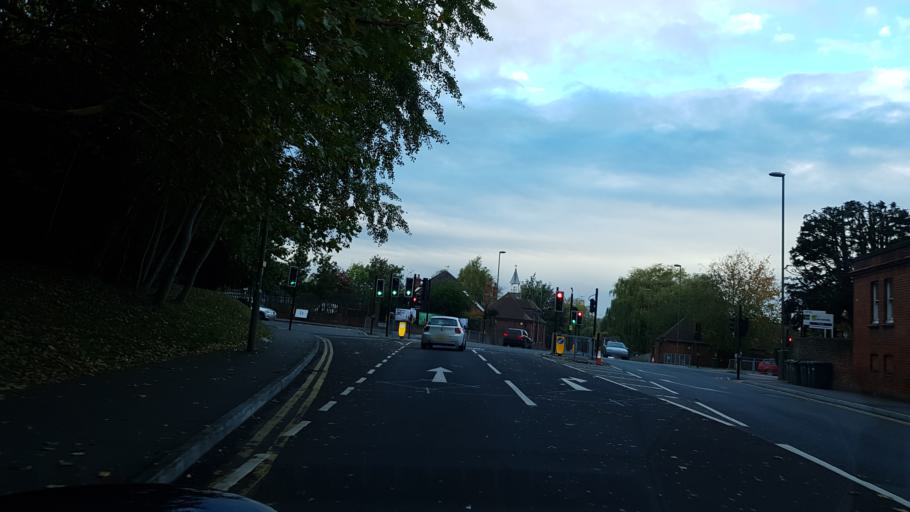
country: GB
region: England
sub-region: Surrey
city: Guildford
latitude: 51.2398
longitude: -0.5705
